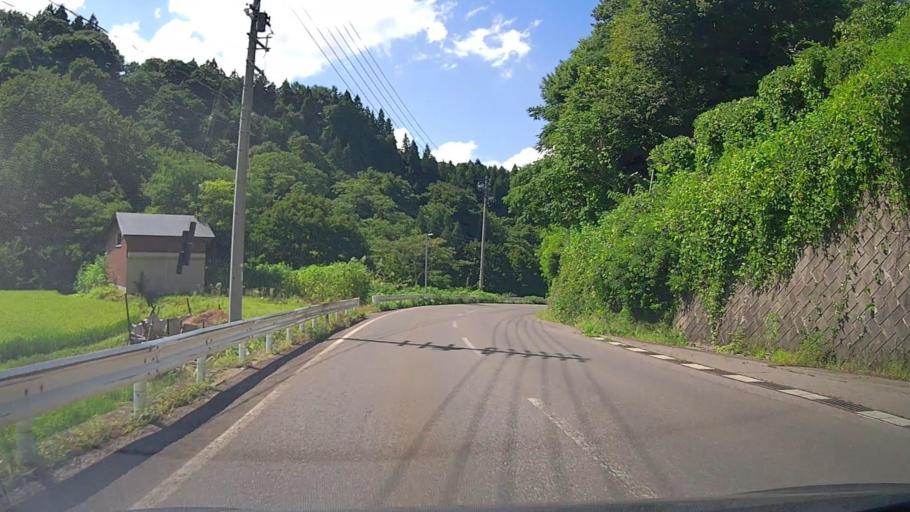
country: JP
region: Nagano
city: Iiyama
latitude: 36.9256
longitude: 138.4250
